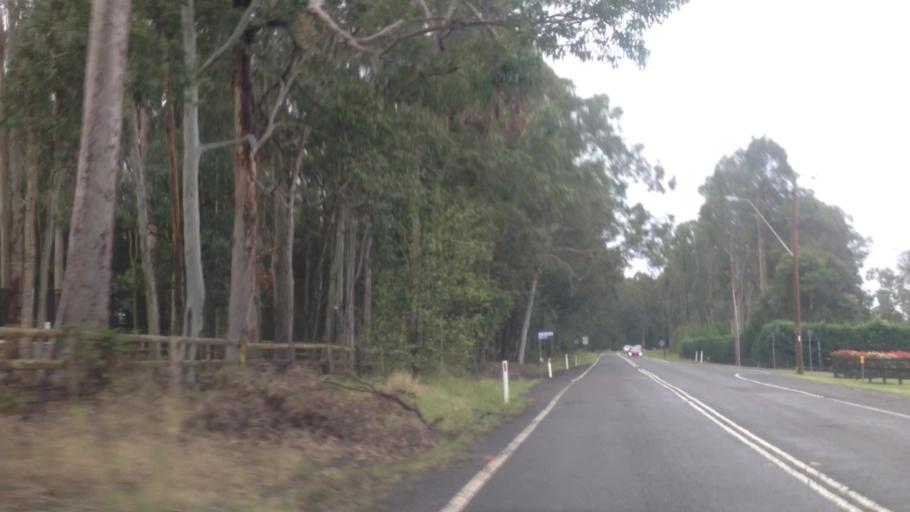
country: AU
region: New South Wales
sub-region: Wyong Shire
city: Little Jilliby
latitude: -33.2555
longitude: 151.3973
